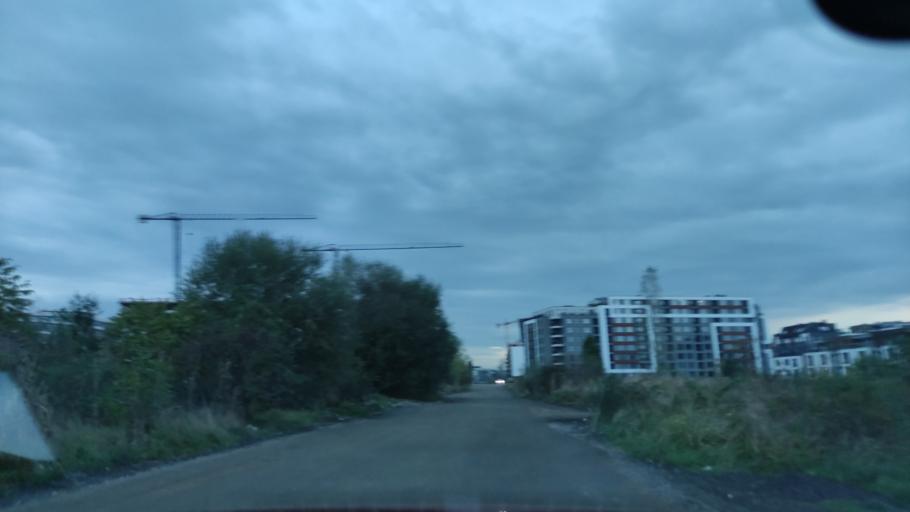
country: BG
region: Sofia-Capital
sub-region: Stolichna Obshtina
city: Sofia
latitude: 42.6536
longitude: 23.2932
